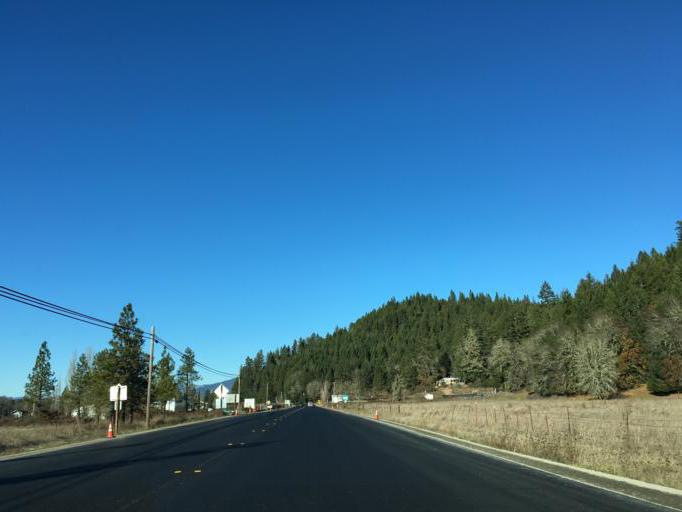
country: US
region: California
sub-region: Mendocino County
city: Laytonville
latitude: 39.6517
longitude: -123.4764
